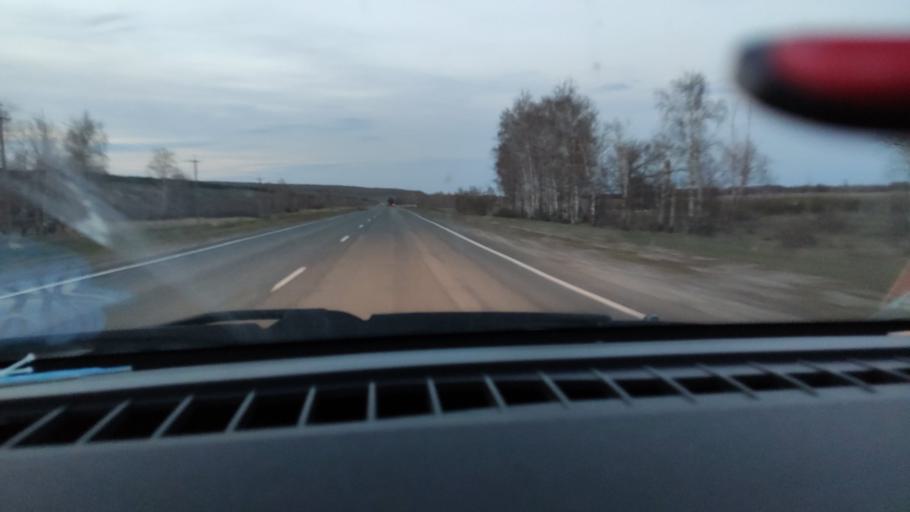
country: RU
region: Saratov
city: Sinodskoye
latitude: 52.0588
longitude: 46.7615
